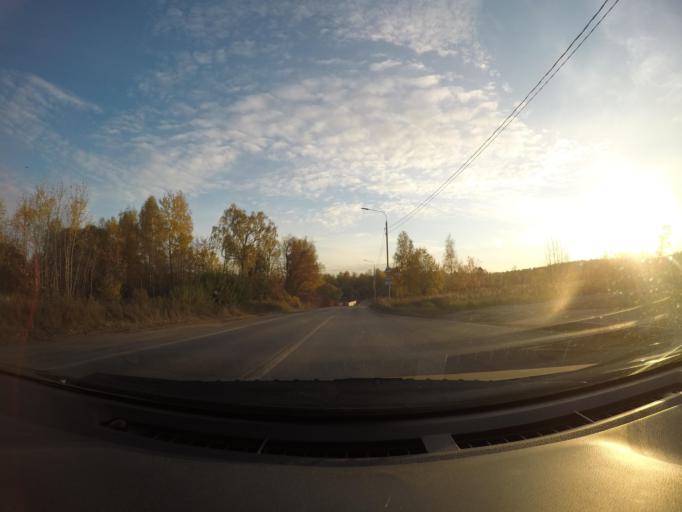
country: RU
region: Moskovskaya
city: Rzhavki
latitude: 55.9741
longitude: 37.2626
